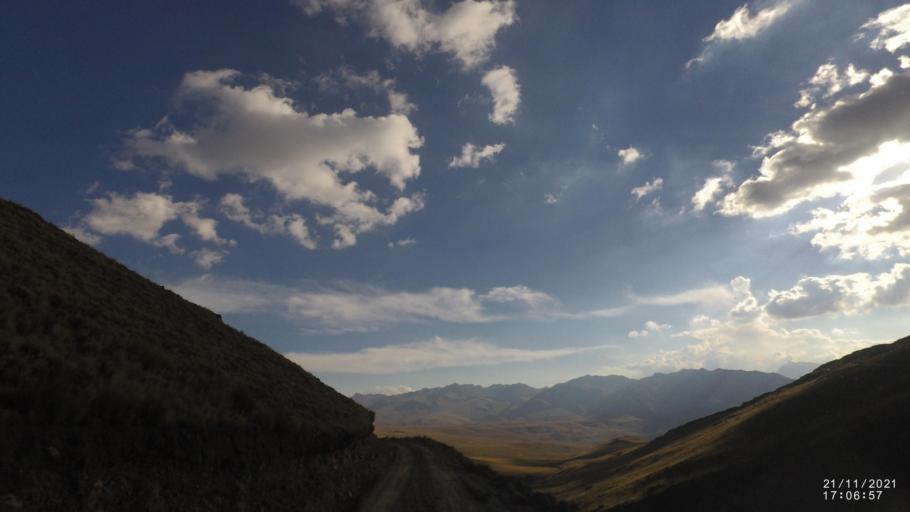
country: BO
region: Cochabamba
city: Cochabamba
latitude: -17.1240
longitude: -66.2593
